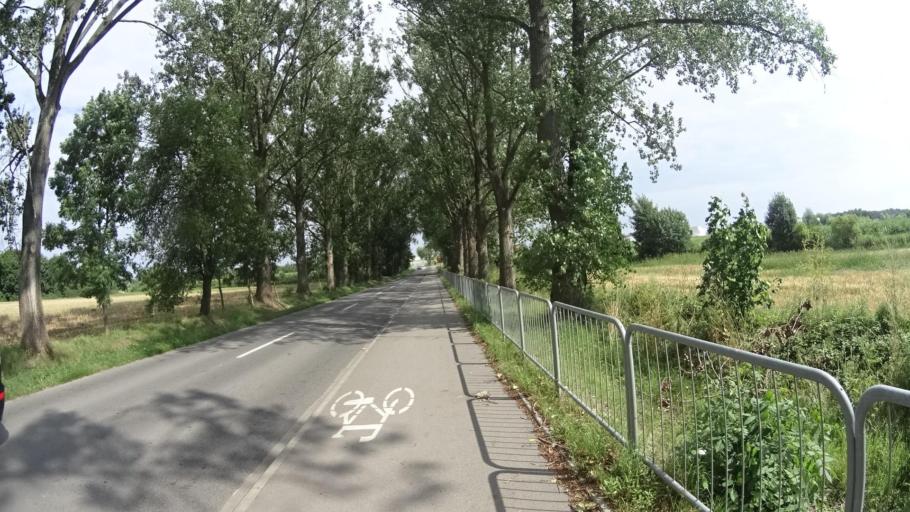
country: PL
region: Masovian Voivodeship
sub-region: Powiat pruszkowski
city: Nadarzyn
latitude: 52.0593
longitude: 20.7859
